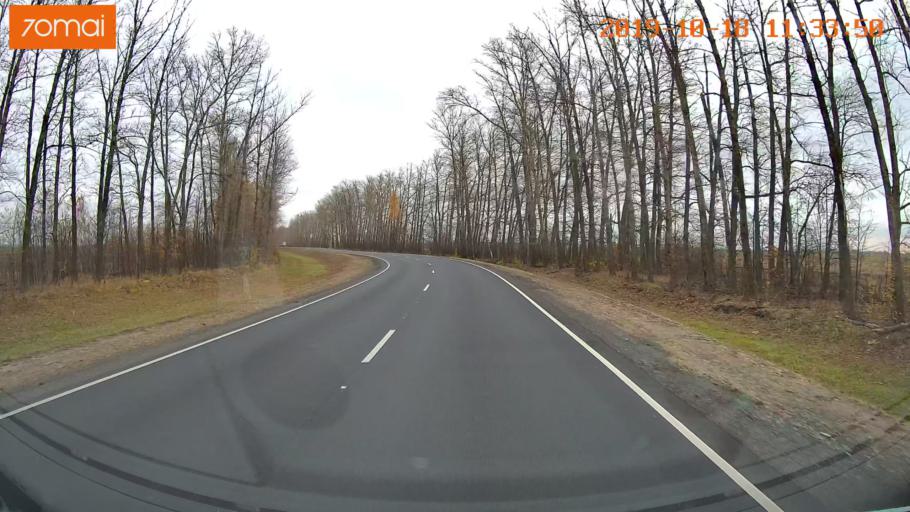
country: RU
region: Rjazan
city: Oktyabr'skiy
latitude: 54.1380
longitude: 38.7499
